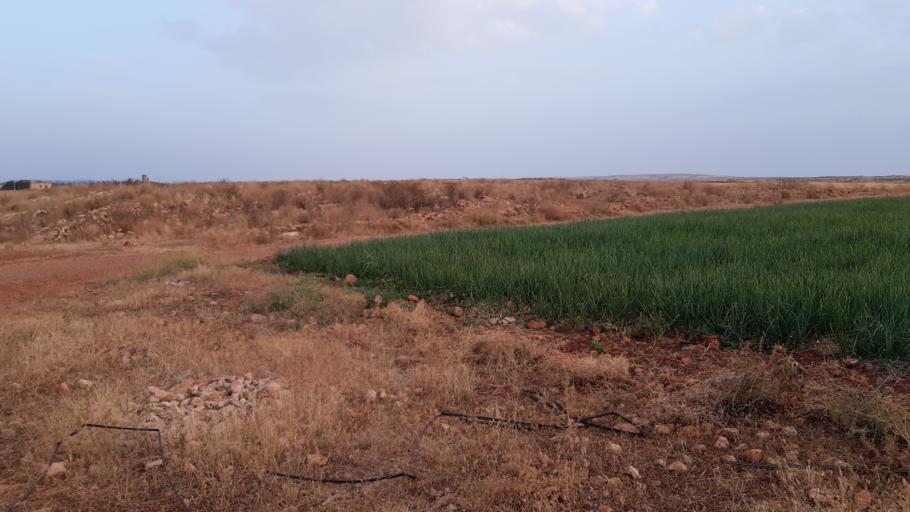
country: MA
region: Meknes-Tafilalet
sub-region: El-Hajeb
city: El Hajeb
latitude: 33.6624
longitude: -5.3597
